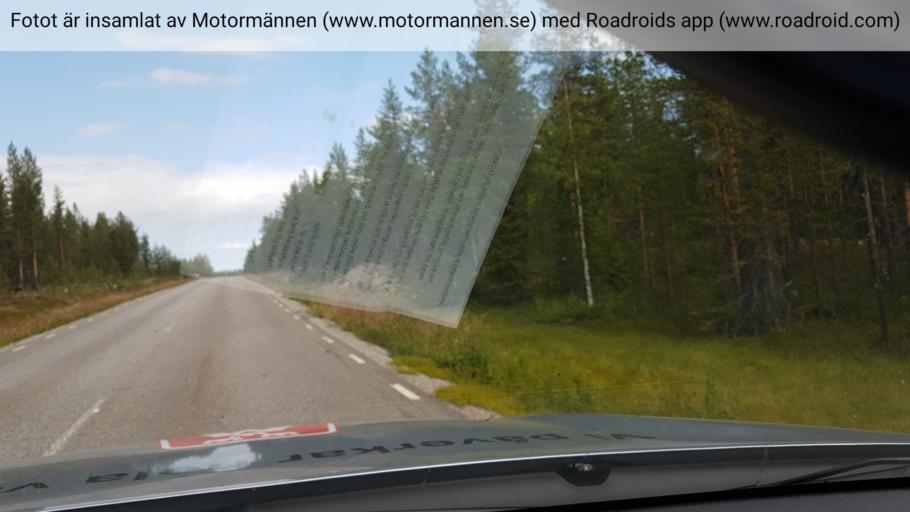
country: SE
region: Vaesterbotten
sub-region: Skelleftea Kommun
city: Boliden
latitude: 65.2941
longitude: 20.2245
